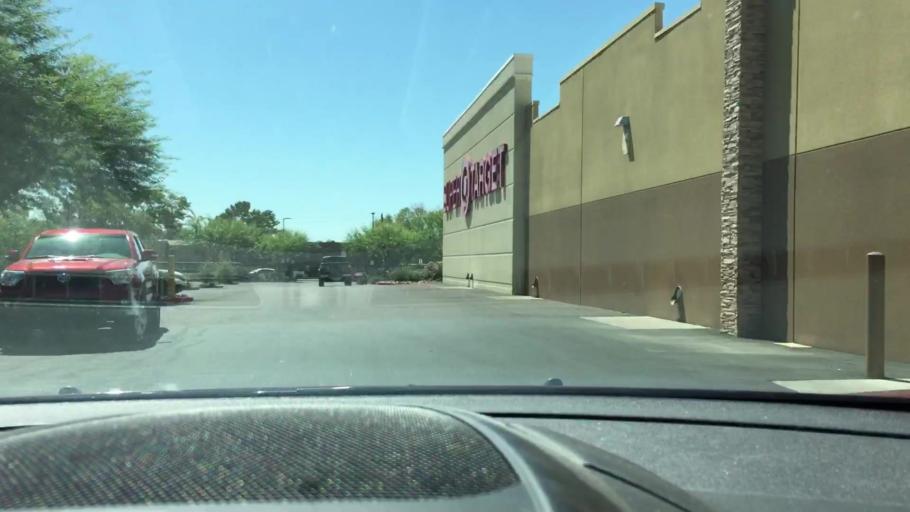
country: US
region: Arizona
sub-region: Maricopa County
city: Phoenix
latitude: 33.5208
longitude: -112.0968
